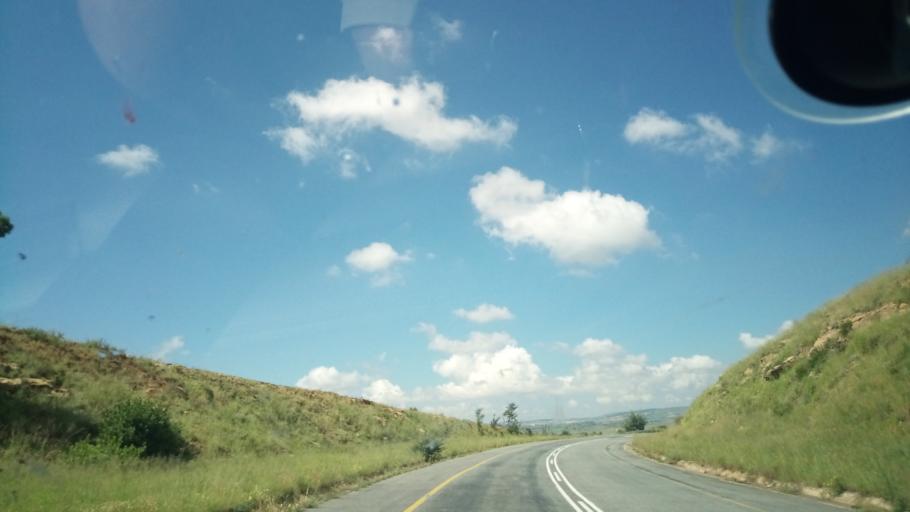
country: ZA
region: Orange Free State
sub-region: Thabo Mofutsanyana District Municipality
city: Ficksburg
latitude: -28.8830
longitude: 27.8667
